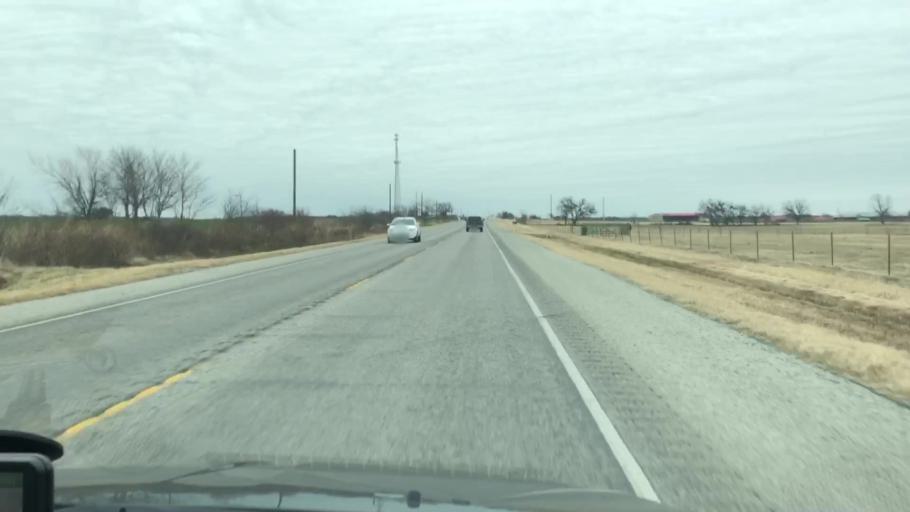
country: US
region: Texas
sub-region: Palo Pinto County
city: Mineral Wells
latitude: 32.9130
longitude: -98.0782
